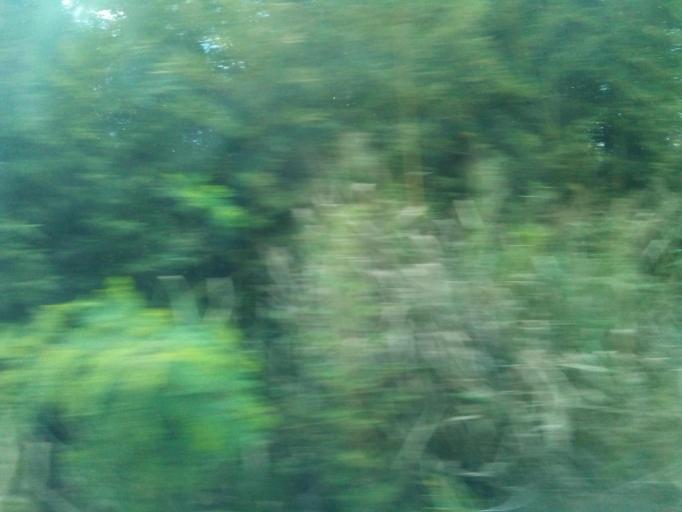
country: BR
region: Minas Gerais
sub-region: Raposos
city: Raposos
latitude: -19.8727
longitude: -43.8449
